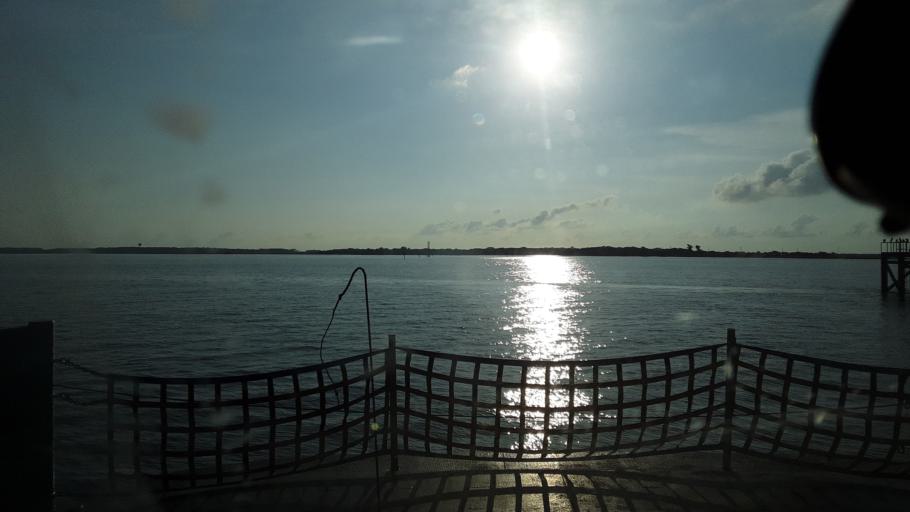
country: US
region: North Carolina
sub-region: New Hanover County
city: Kure Beach
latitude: 33.9617
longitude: -77.9504
